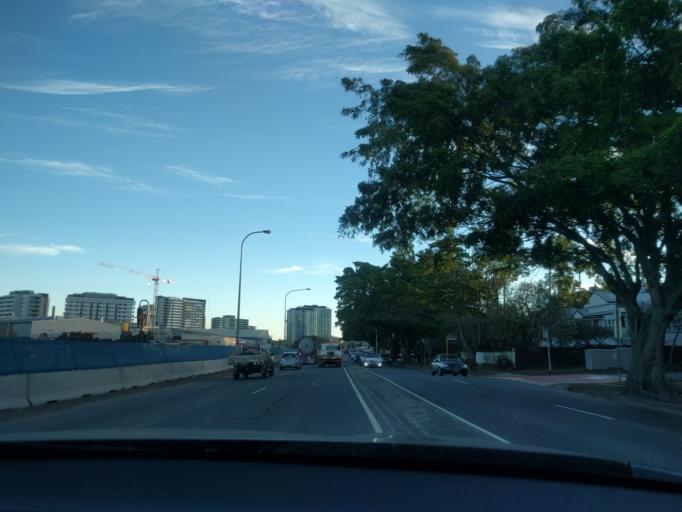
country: AU
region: Queensland
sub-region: Brisbane
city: Ascot
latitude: -27.4363
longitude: 153.0740
